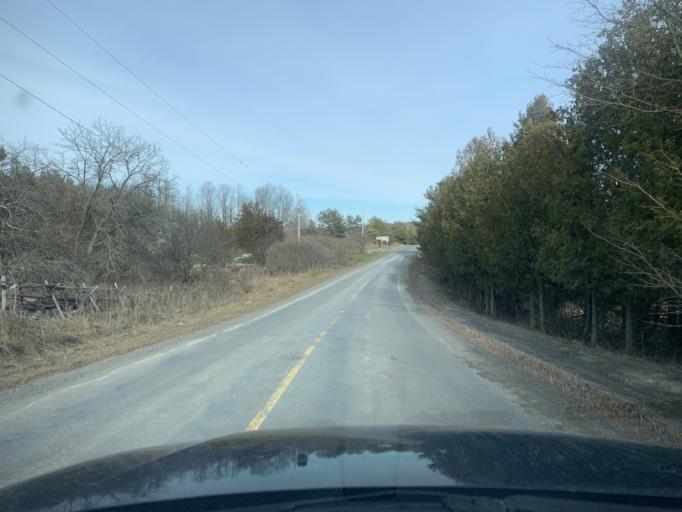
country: CA
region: Ontario
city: Greater Napanee
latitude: 44.4414
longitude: -77.0768
